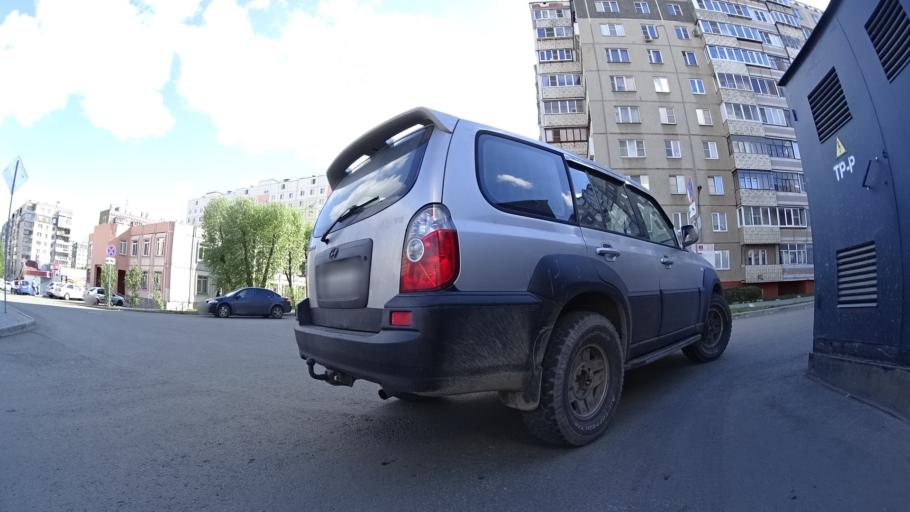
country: RU
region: Chelyabinsk
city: Roshchino
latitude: 55.1801
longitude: 61.2937
